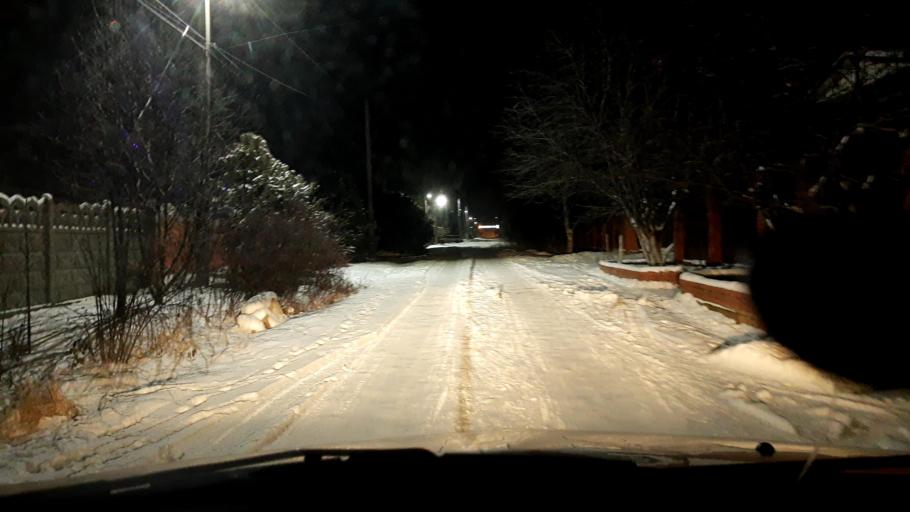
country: RU
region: Bashkortostan
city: Ufa
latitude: 54.6225
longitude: 55.9200
